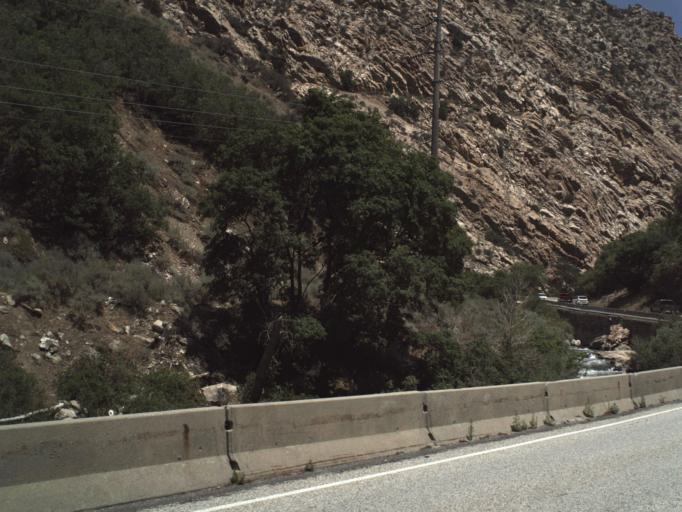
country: US
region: Utah
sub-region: Weber County
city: Ogden
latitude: 41.2369
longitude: -111.9193
